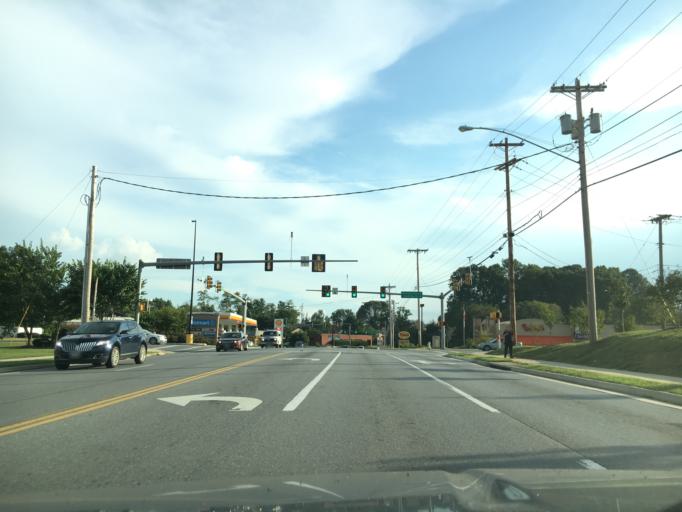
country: US
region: Virginia
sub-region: City of Lynchburg
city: West Lynchburg
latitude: 37.4124
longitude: -79.2122
